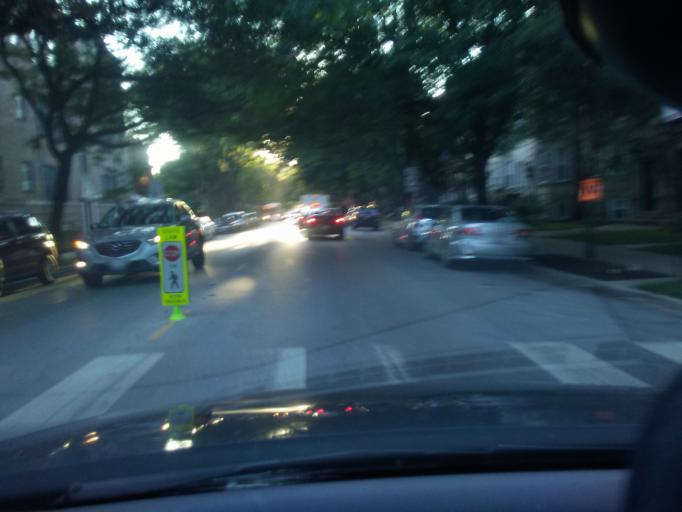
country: US
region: Illinois
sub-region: Cook County
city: Evanston
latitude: 41.9762
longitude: -87.6635
